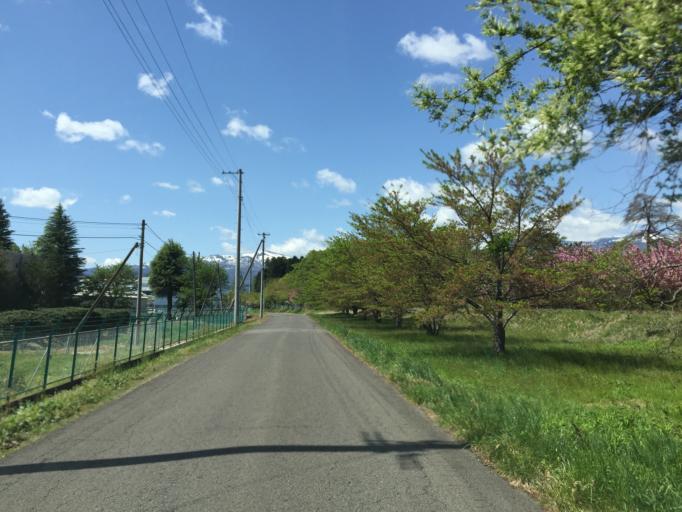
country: JP
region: Fukushima
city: Fukushima-shi
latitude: 37.7425
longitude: 140.4006
